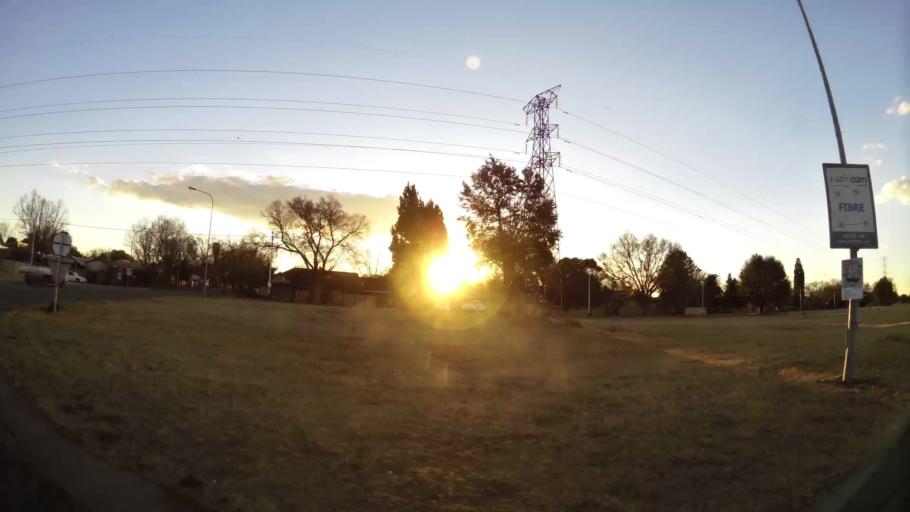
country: ZA
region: North-West
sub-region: Dr Kenneth Kaunda District Municipality
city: Potchefstroom
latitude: -26.7212
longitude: 27.1032
